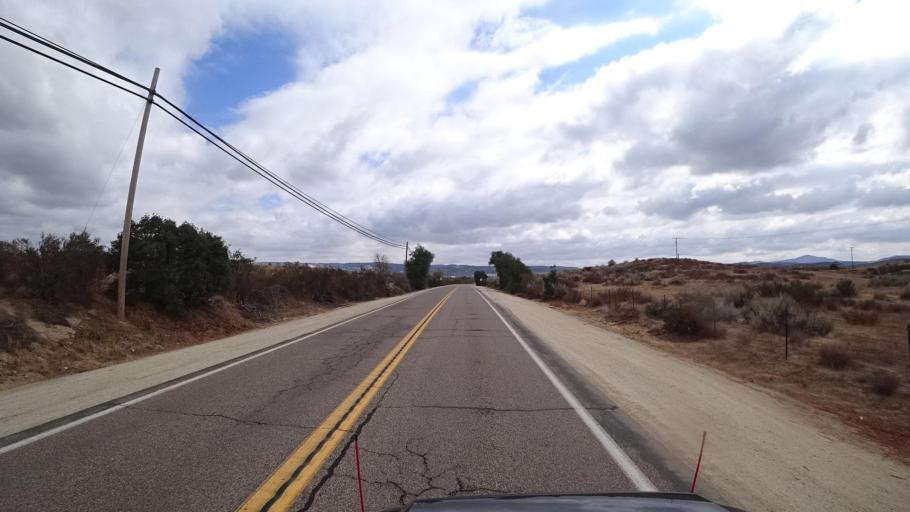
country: US
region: California
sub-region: San Diego County
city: Campo
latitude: 32.6402
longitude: -116.4818
